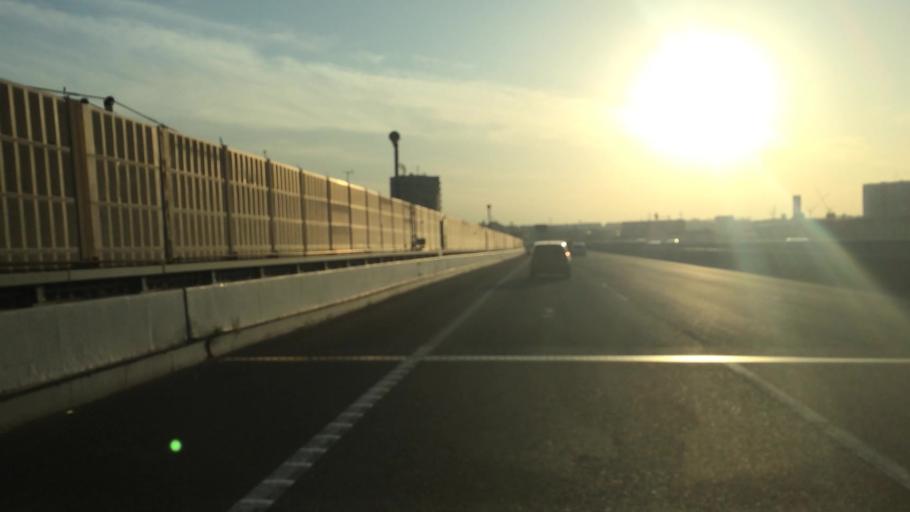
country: JP
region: Tokyo
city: Chofugaoka
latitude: 35.5965
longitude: 139.6298
